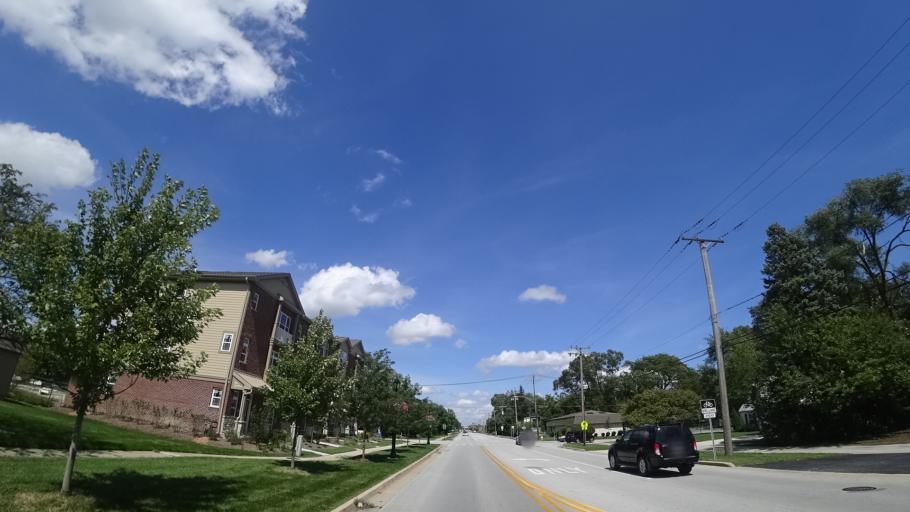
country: US
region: Illinois
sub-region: Cook County
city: Tinley Park
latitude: 41.5655
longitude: -87.7841
